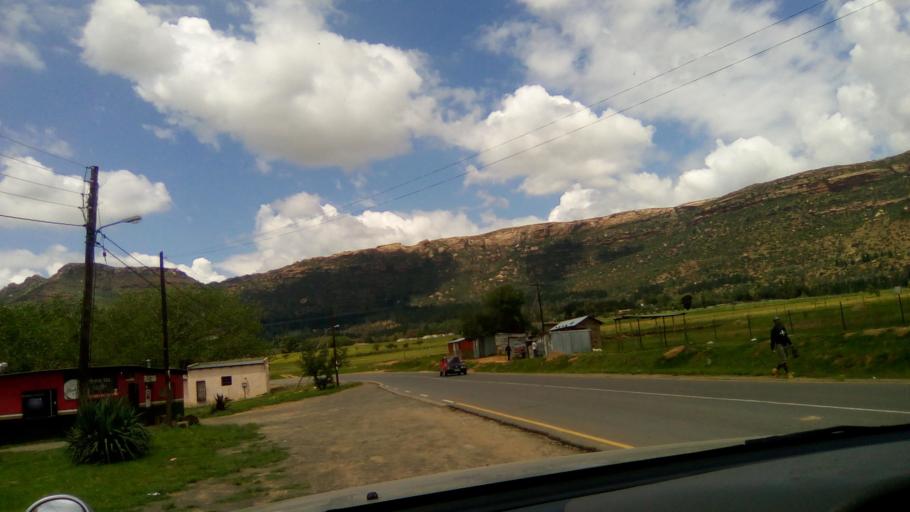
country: LS
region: Maseru
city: Nako
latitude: -29.6227
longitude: 27.4973
